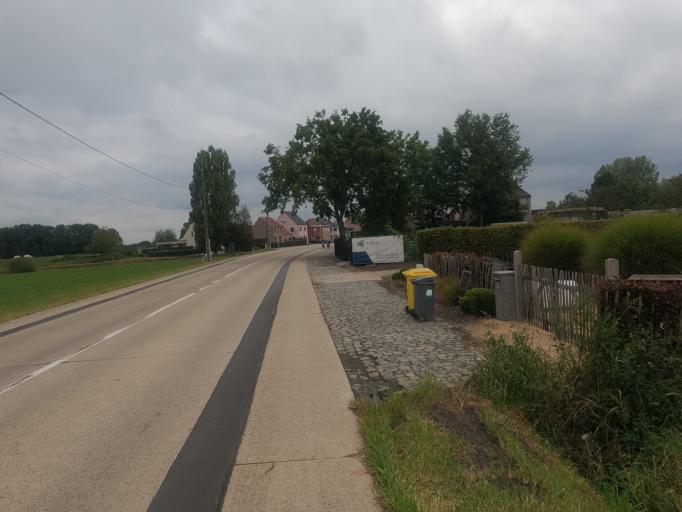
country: BE
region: Flanders
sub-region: Provincie Antwerpen
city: Berlaar
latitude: 51.1292
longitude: 4.6940
